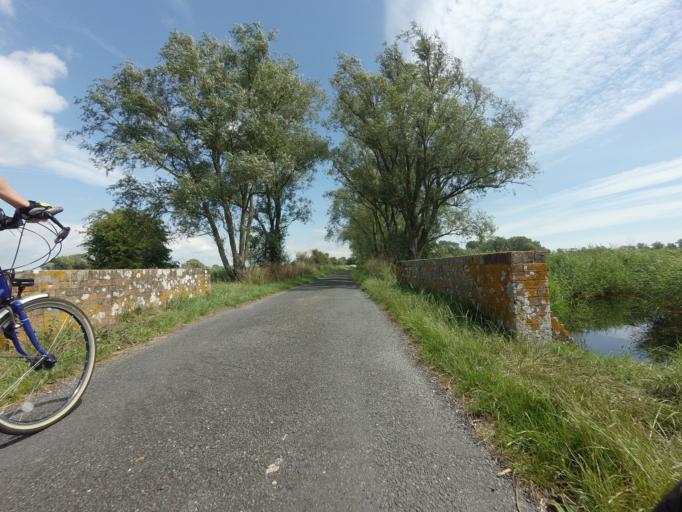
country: GB
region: England
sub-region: Kent
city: Stone
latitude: 50.9992
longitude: 0.8190
